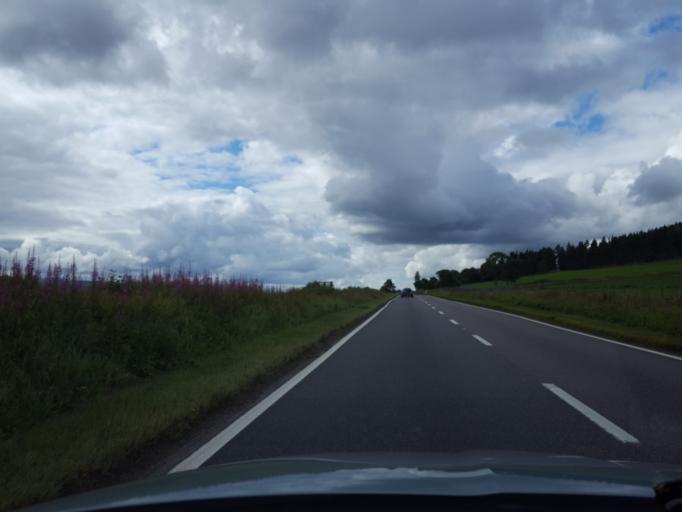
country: GB
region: Scotland
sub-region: Highland
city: Grantown on Spey
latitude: 57.3129
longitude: -3.6304
